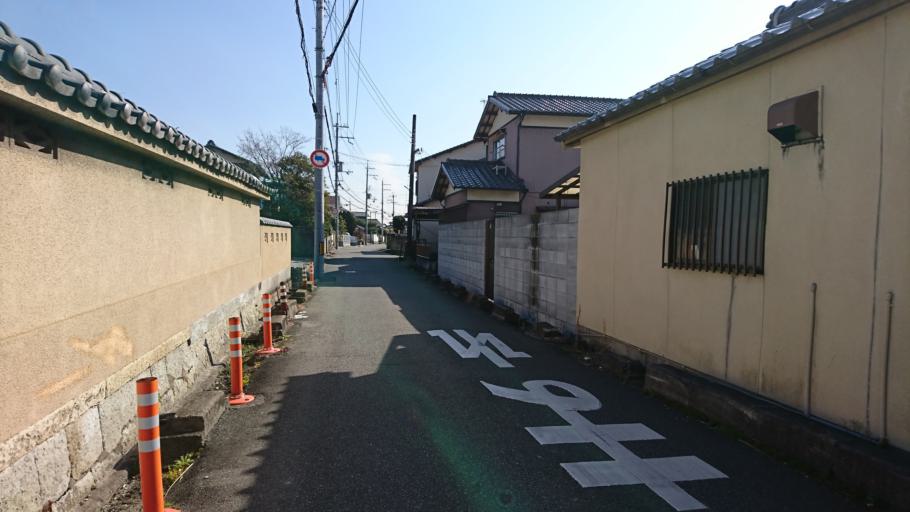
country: JP
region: Hyogo
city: Kakogawacho-honmachi
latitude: 34.7941
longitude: 134.8274
